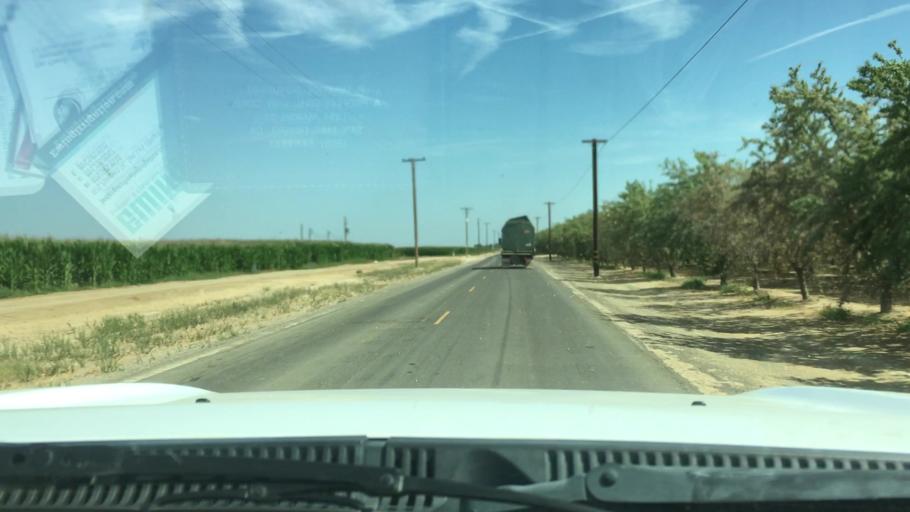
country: US
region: California
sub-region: Kern County
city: Shafter
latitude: 35.4768
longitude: -119.3680
